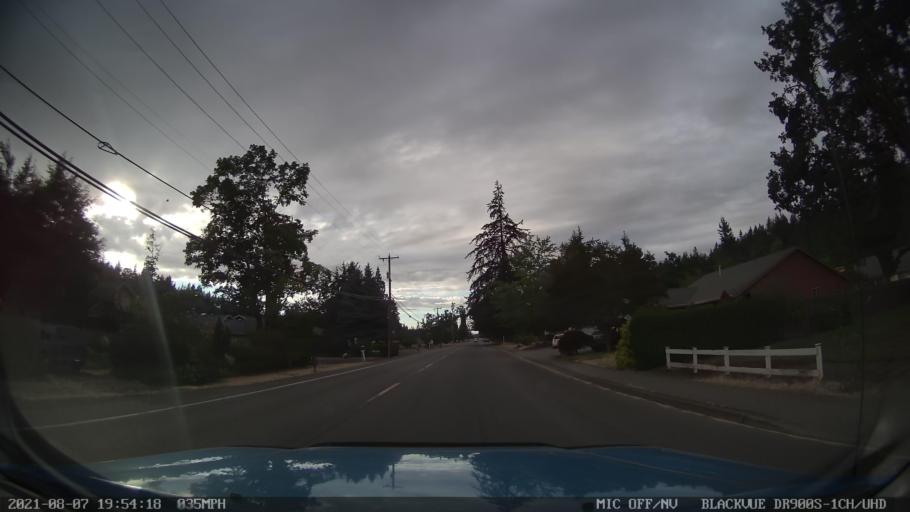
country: US
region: Oregon
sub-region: Marion County
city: Silverton
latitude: 44.9939
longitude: -122.7725
